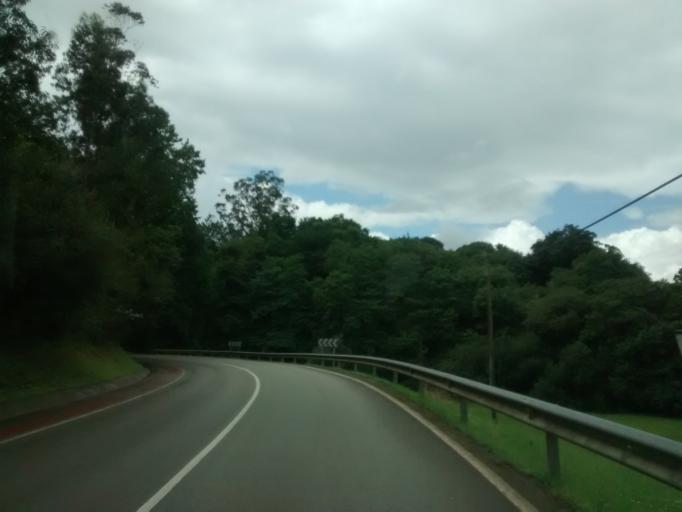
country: ES
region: Cantabria
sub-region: Provincia de Cantabria
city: Entrambasaguas
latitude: 43.3734
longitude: -3.6873
